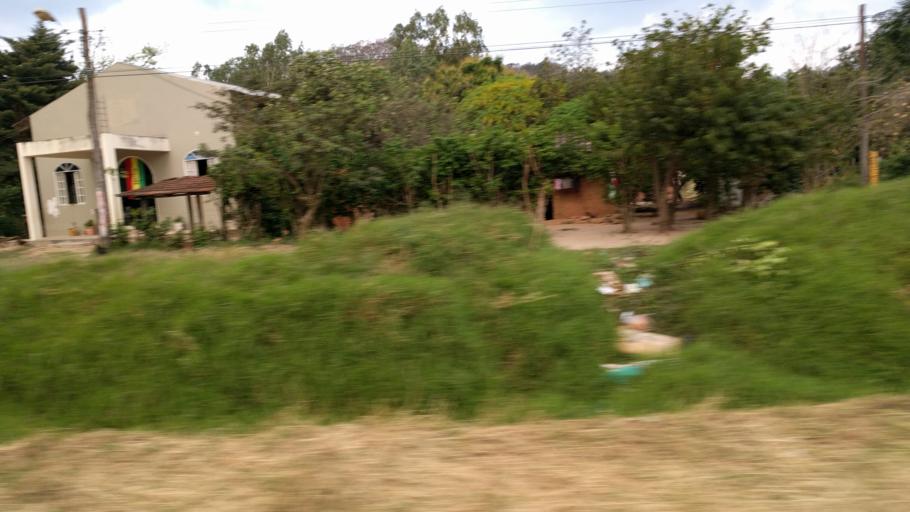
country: BO
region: Santa Cruz
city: Jorochito
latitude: -18.0827
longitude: -63.4493
